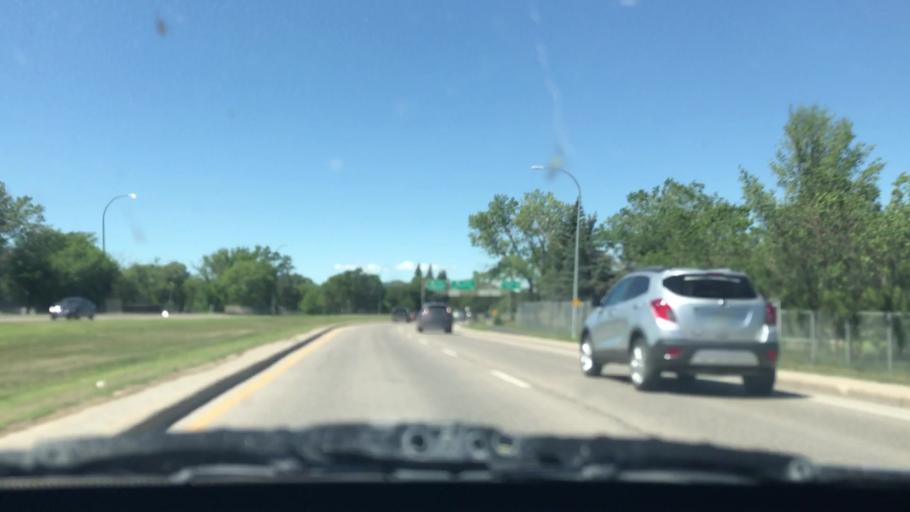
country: CA
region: Manitoba
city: Winnipeg
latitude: 49.8517
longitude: -97.1231
